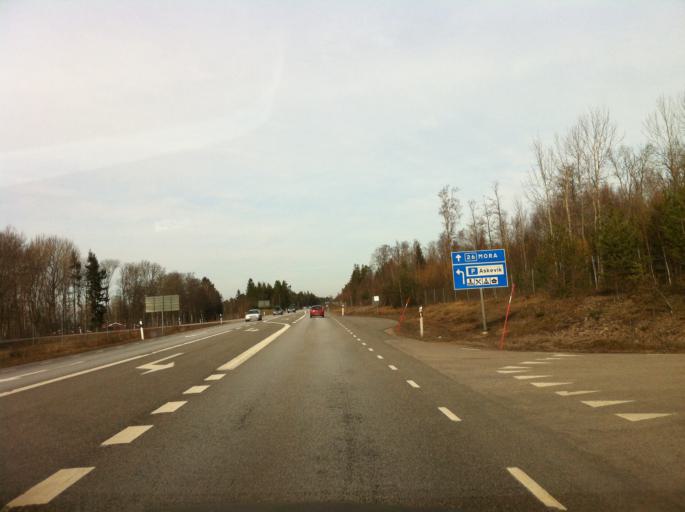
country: SE
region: Vaestra Goetaland
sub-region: Gullspangs Kommun
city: Gullspang
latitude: 58.8880
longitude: 14.0143
